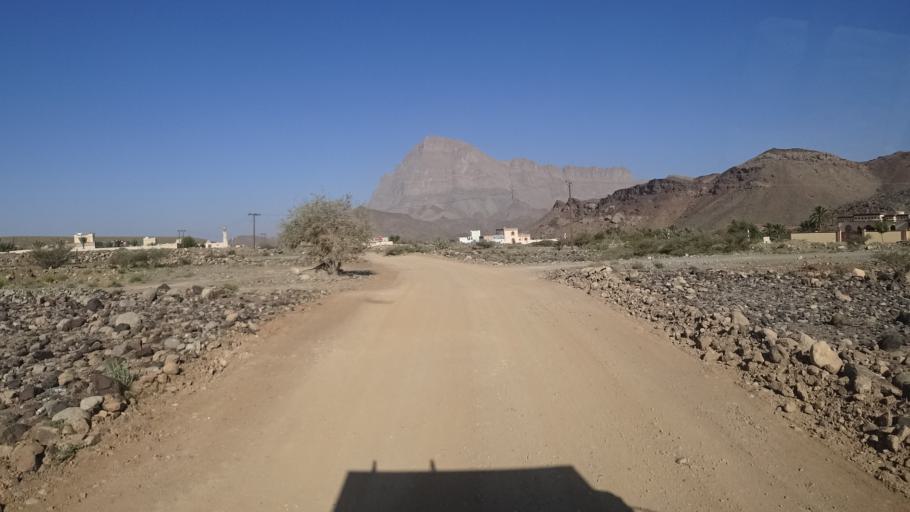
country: OM
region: Muhafazat ad Dakhiliyah
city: Bahla'
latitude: 23.2258
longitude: 57.0594
